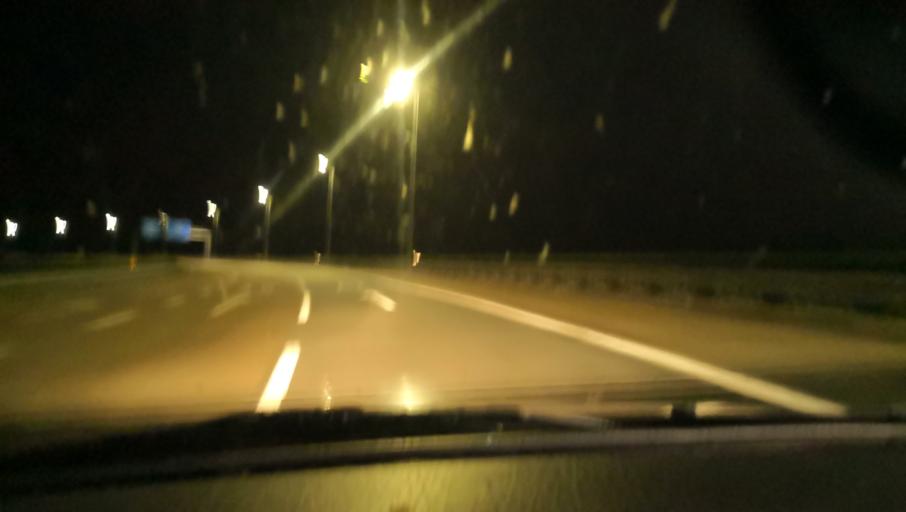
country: PT
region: Evora
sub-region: Vendas Novas
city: Vendas Novas
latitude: 38.6048
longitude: -8.6491
